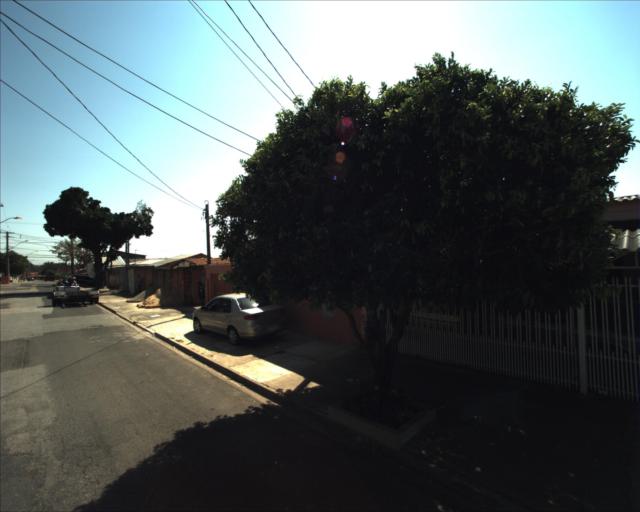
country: BR
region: Sao Paulo
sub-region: Sorocaba
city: Sorocaba
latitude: -23.4620
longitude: -47.4912
